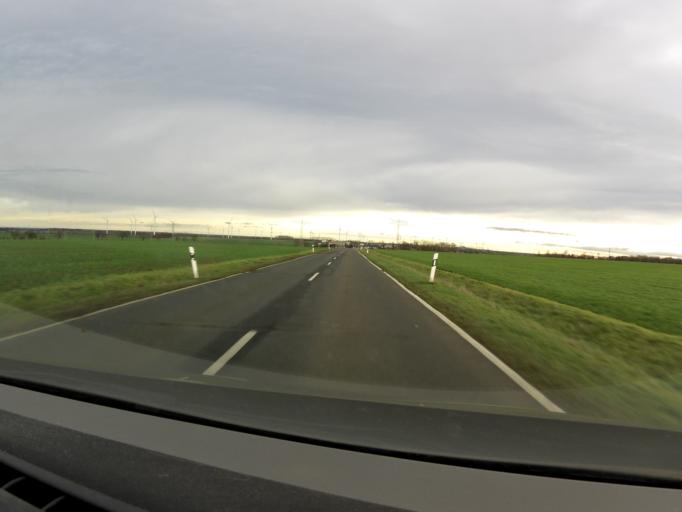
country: DE
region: Saxony-Anhalt
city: Gerbstedt
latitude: 51.6424
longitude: 11.6089
